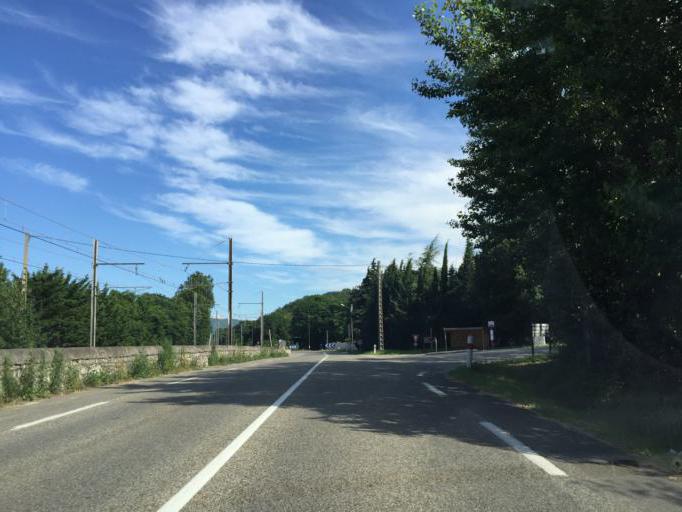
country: FR
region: Rhone-Alpes
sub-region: Departement de l'Ardeche
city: Le Pouzin
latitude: 44.7214
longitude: 4.7485
